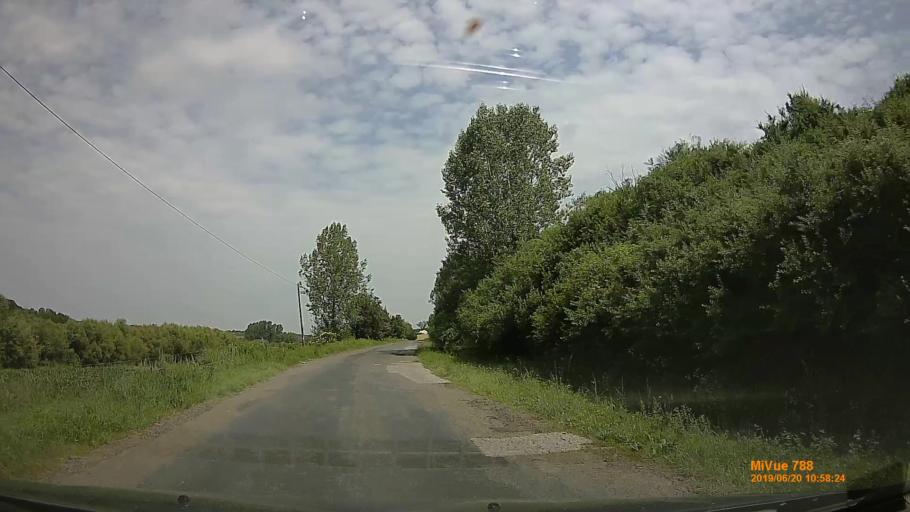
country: HU
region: Baranya
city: Mecseknadasd
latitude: 46.1595
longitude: 18.5165
